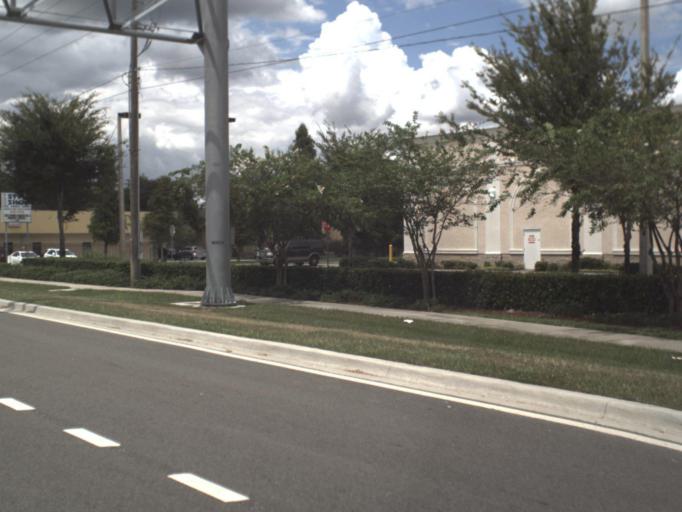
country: US
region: Florida
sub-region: Polk County
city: Bartow
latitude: 27.9042
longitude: -81.8441
